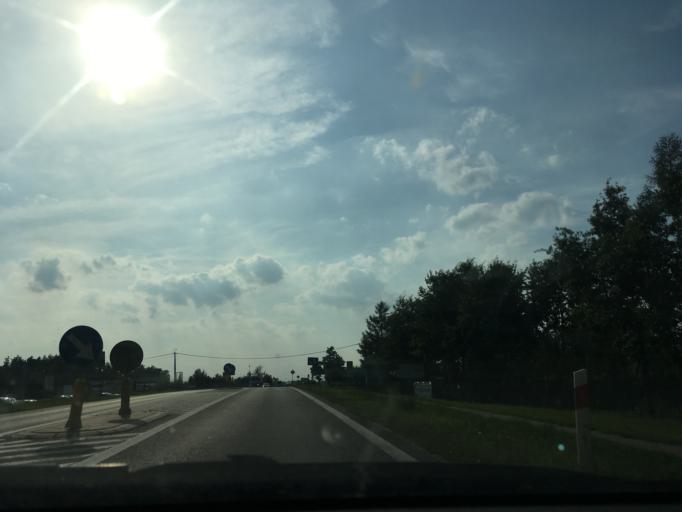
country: PL
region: Podlasie
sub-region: Powiat bialostocki
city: Wasilkow
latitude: 53.1253
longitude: 23.2500
